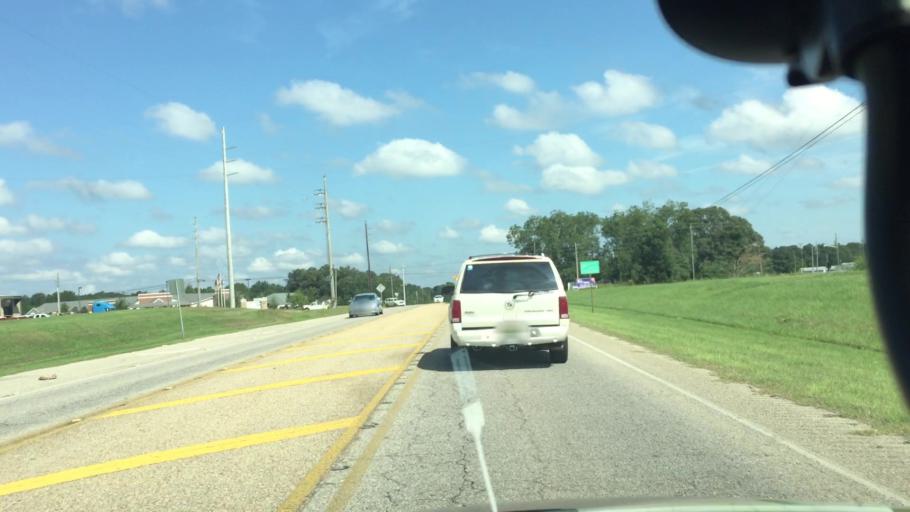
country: US
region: Alabama
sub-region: Coffee County
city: Enterprise
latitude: 31.3589
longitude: -85.8666
